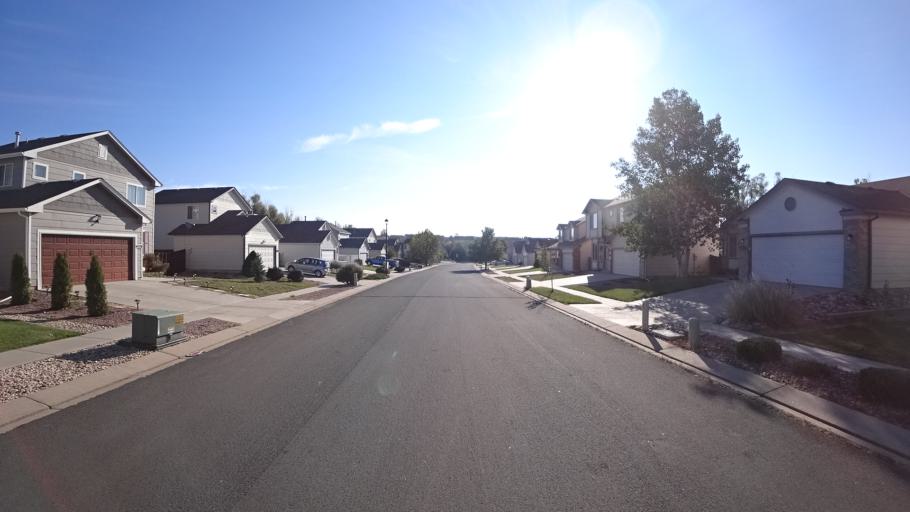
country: US
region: Colorado
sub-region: El Paso County
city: Cimarron Hills
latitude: 38.8907
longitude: -104.6933
